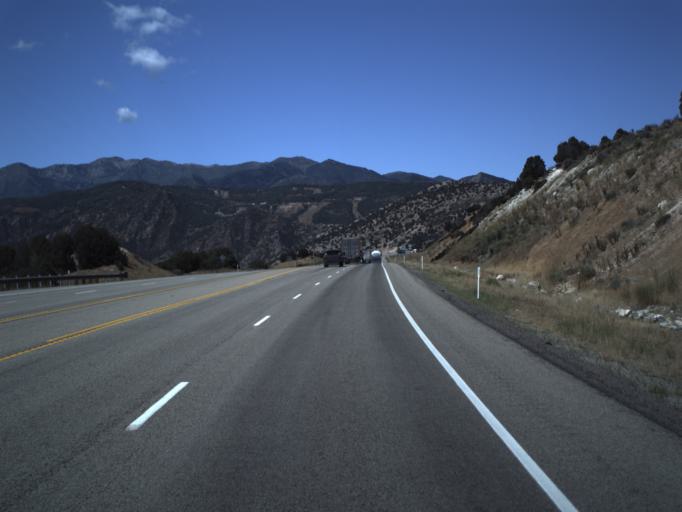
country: US
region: Utah
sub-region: Utah County
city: Mapleton
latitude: 39.9952
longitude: -111.4644
